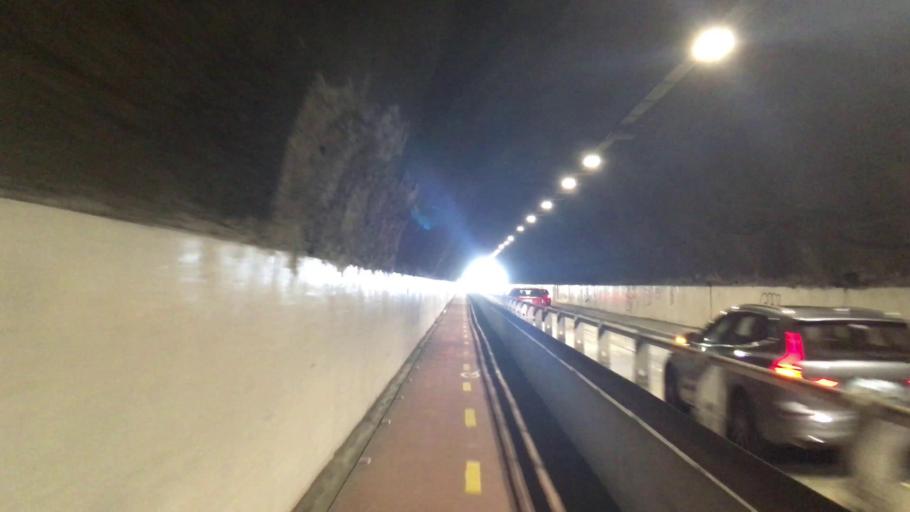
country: BR
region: Rio de Janeiro
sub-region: Rio De Janeiro
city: Rio de Janeiro
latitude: -23.0109
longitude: -43.2895
